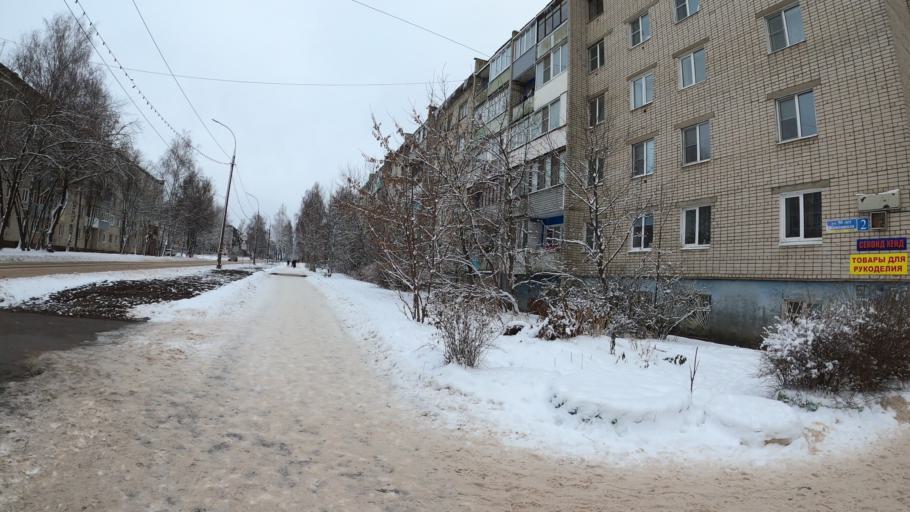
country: RU
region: Jaroslavl
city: Pereslavl'-Zalesskiy
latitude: 56.7513
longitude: 38.8729
